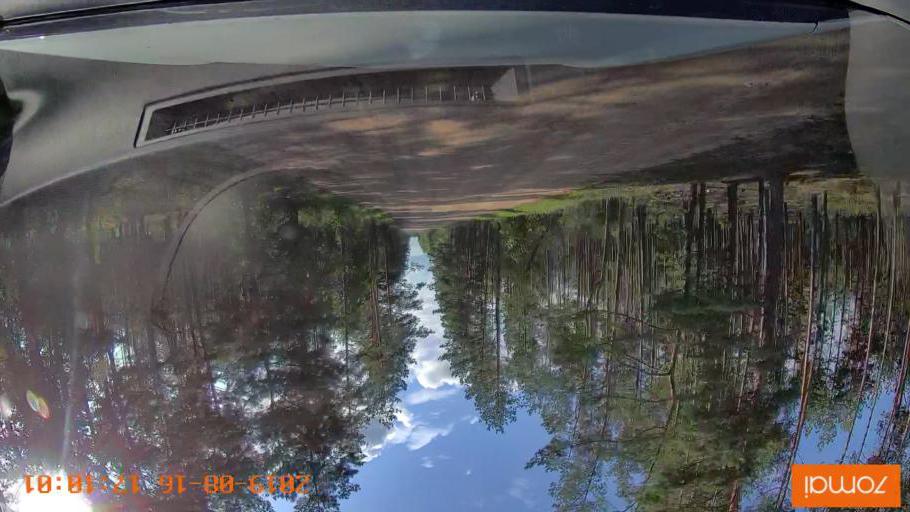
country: BY
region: Mogilev
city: Hlusha
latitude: 53.2057
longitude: 28.9220
